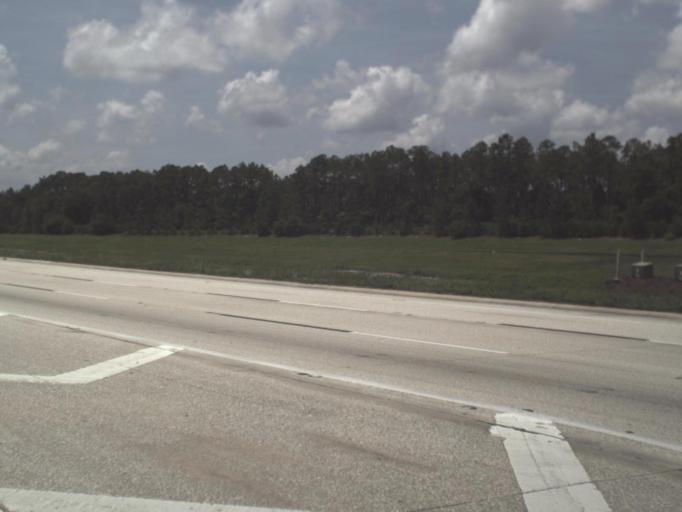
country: US
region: Florida
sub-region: Saint Johns County
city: Fruit Cove
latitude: 30.1671
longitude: -81.5652
